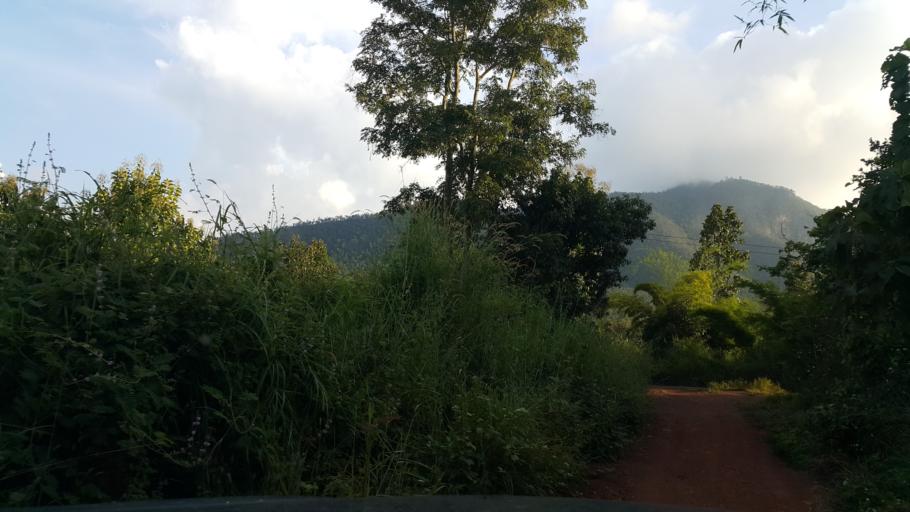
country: TH
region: Chiang Mai
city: Mae On
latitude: 18.7424
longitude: 99.2480
